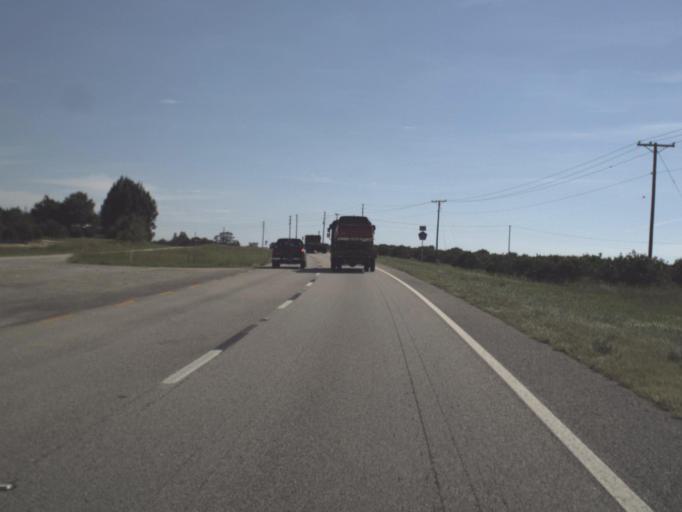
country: US
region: Florida
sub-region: Highlands County
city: Lake Placid
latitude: 27.3369
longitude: -81.3859
